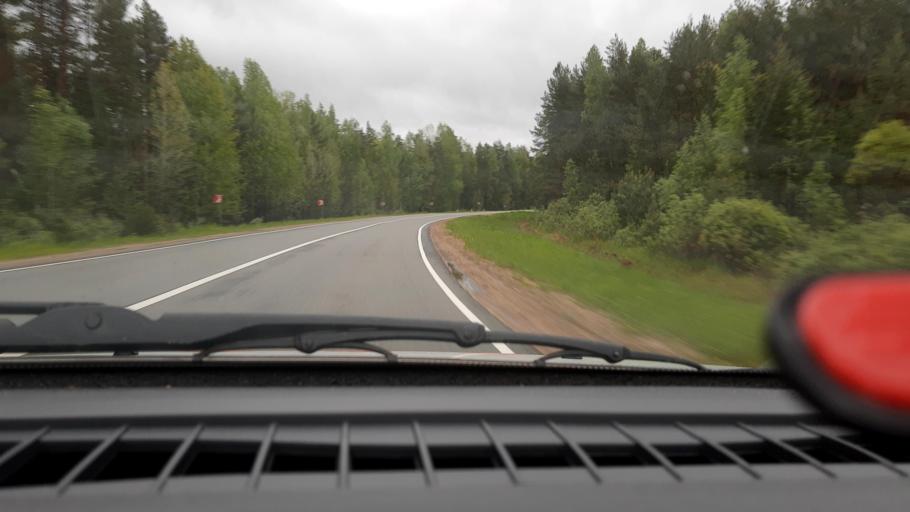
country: RU
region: Nizjnij Novgorod
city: Krasnyye Baki
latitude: 57.2117
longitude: 45.4625
